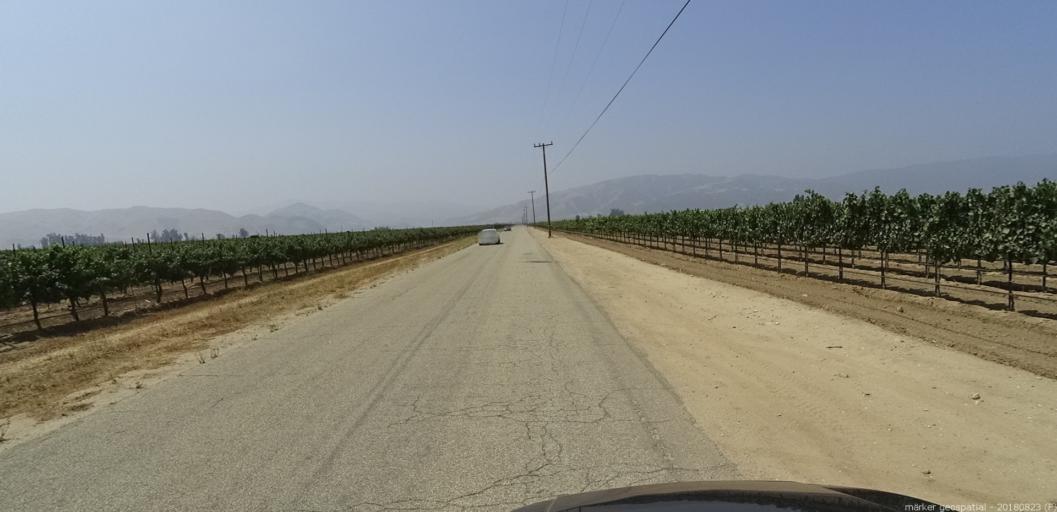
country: US
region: California
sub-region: Monterey County
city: Greenfield
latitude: 36.3274
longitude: -121.2630
